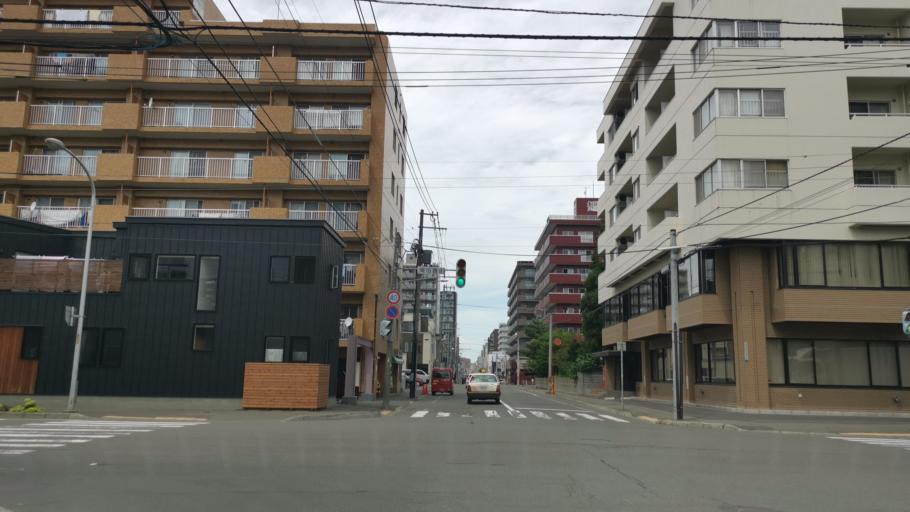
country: JP
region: Hokkaido
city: Sapporo
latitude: 43.0375
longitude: 141.3475
